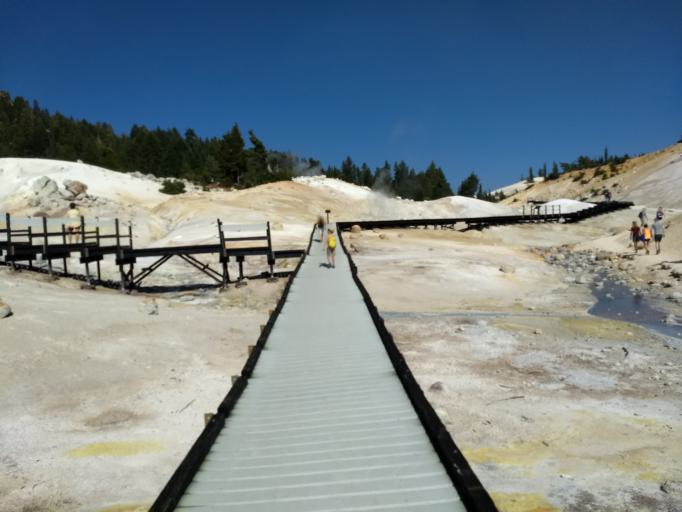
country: US
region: California
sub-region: Plumas County
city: Chester
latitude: 40.4575
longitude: -121.5023
